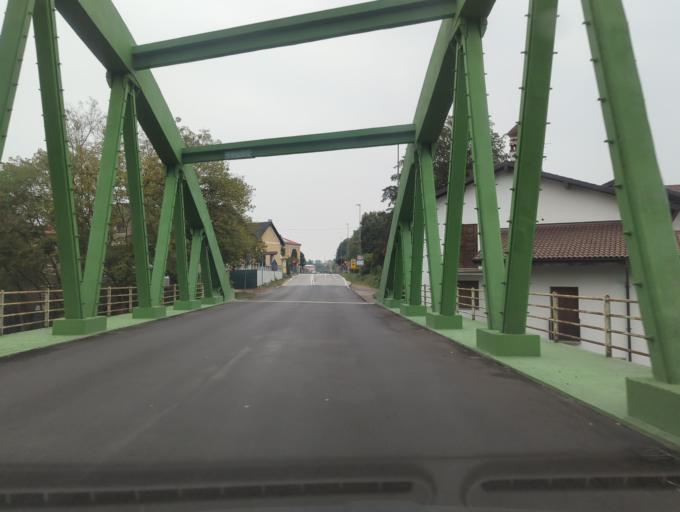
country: IT
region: Lombardy
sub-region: Citta metropolitana di Milano
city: Turbigo
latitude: 45.5309
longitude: 8.7303
